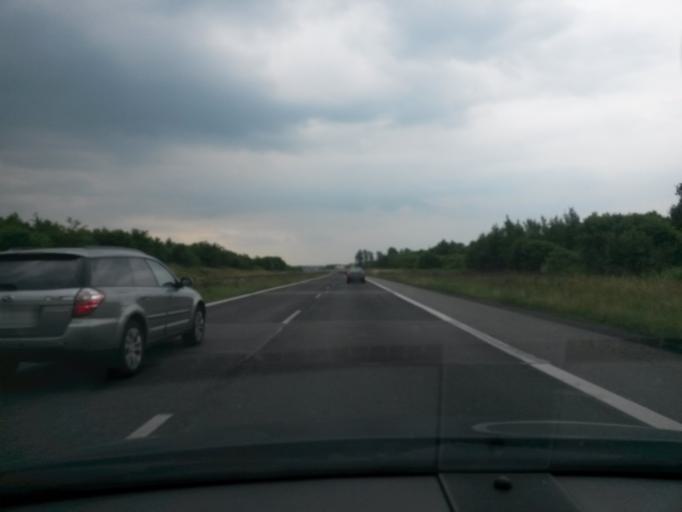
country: PL
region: Silesian Voivodeship
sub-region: Powiat czestochowski
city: Borowno
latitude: 50.9474
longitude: 19.2399
